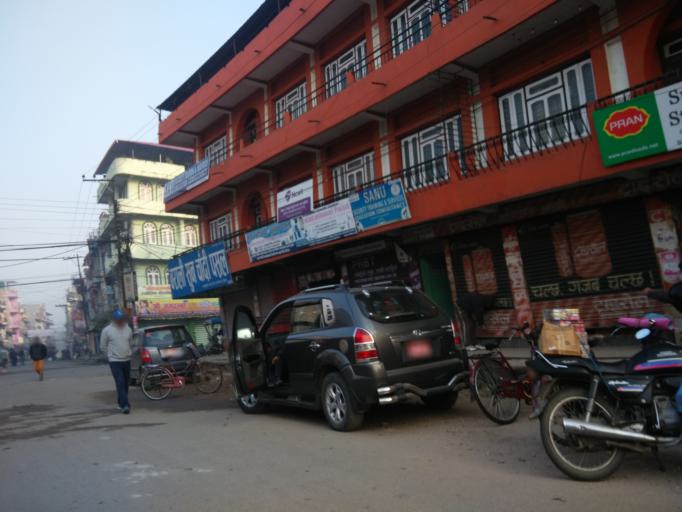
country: NP
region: Central Region
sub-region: Narayani Zone
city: Bharatpur
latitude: 27.6972
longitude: 84.4251
